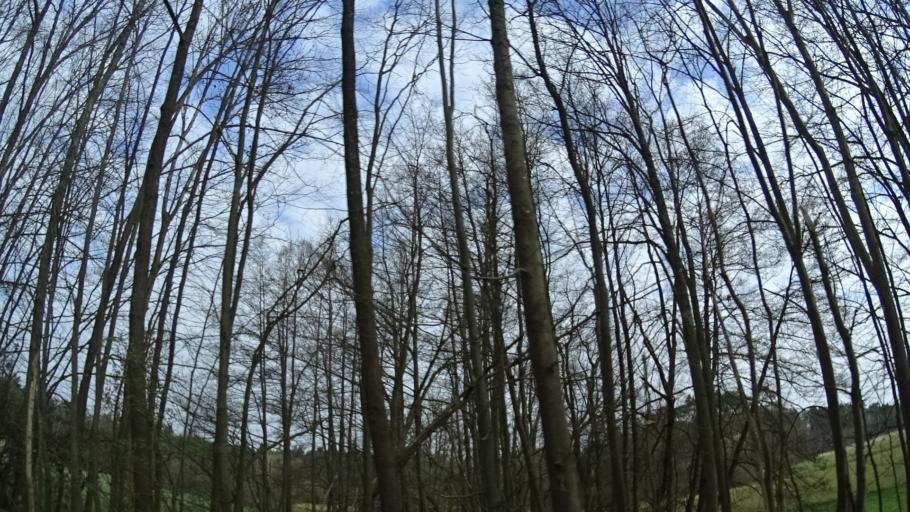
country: DE
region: Bavaria
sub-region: Regierungsbezirk Mittelfranken
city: Winkelhaid
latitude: 49.4150
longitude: 11.2604
